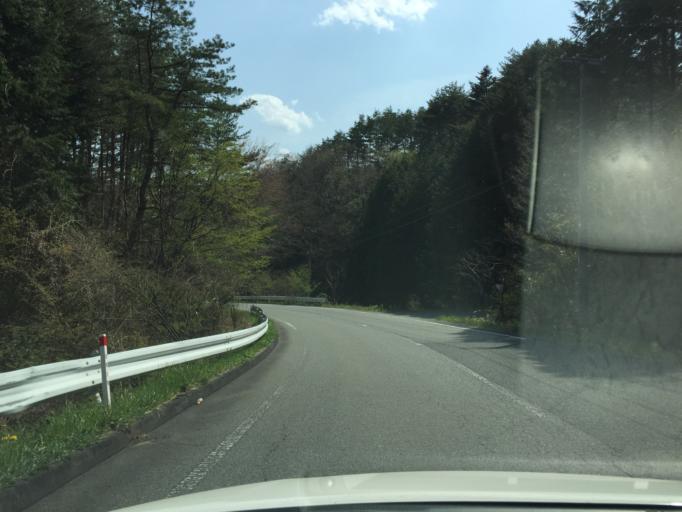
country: JP
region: Fukushima
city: Namie
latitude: 37.3787
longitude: 140.8008
